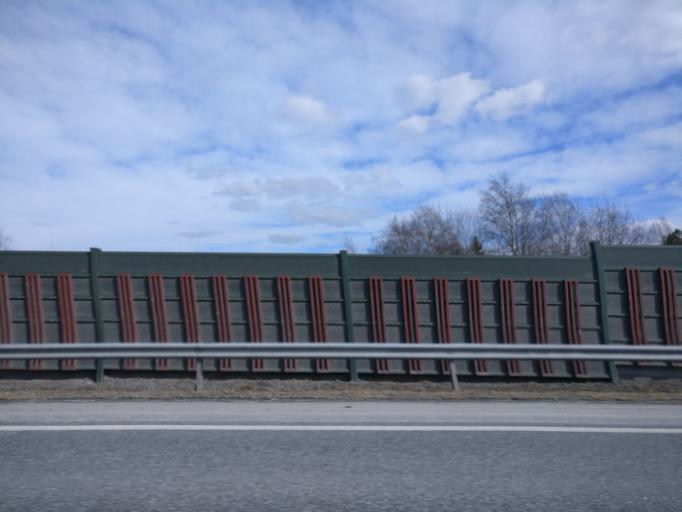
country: FI
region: Pirkanmaa
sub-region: Tampere
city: Lempaeaelae
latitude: 61.3877
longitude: 23.7892
